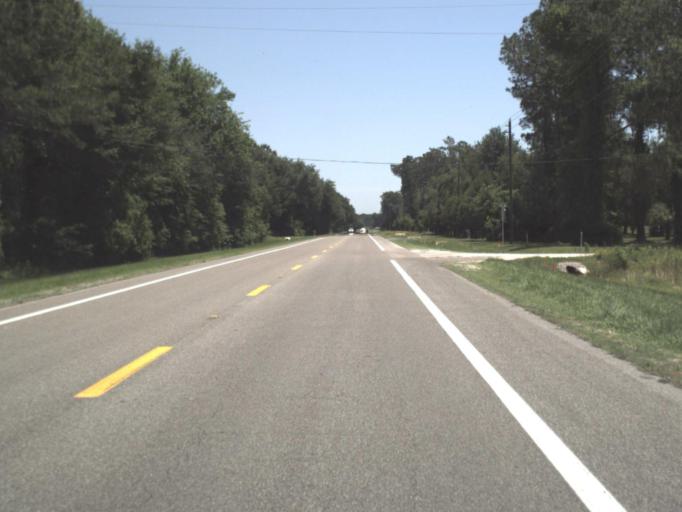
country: US
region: Florida
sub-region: Suwannee County
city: Wellborn
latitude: 30.2363
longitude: -82.8456
